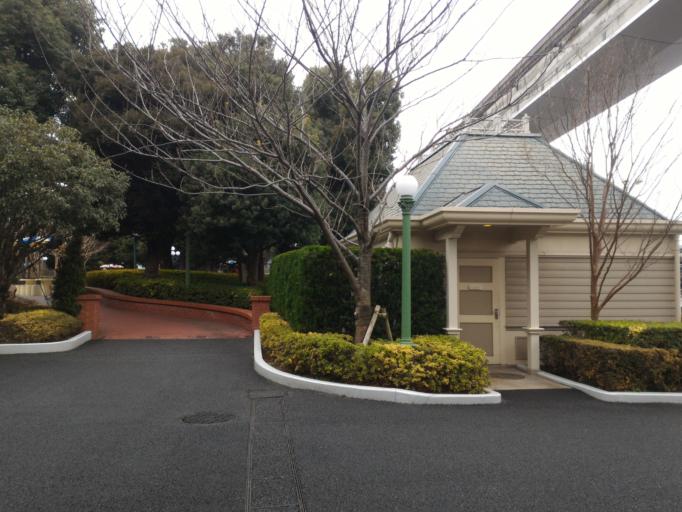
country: JP
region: Tokyo
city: Urayasu
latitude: 35.6358
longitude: 139.8811
